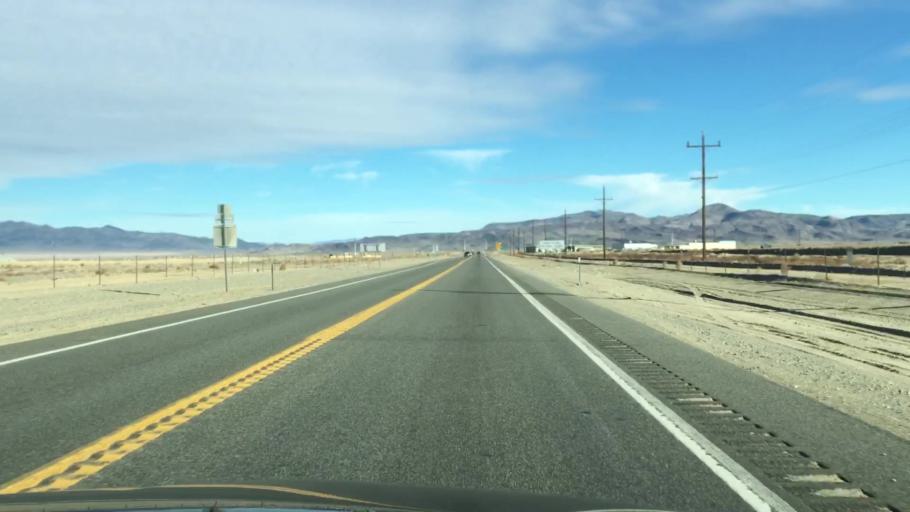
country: US
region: Nevada
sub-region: Mineral County
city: Hawthorne
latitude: 38.5245
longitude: -118.6041
